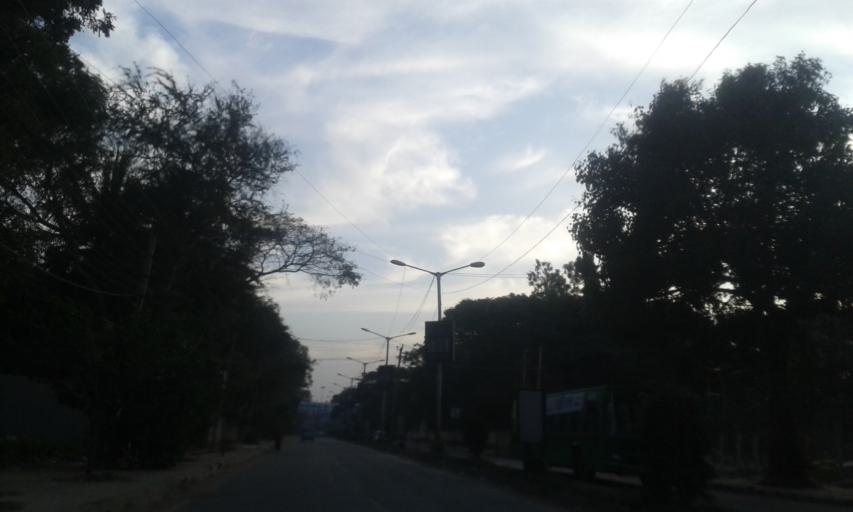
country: IN
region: Karnataka
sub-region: Bangalore Rural
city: Hoskote
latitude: 12.9885
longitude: 77.7544
